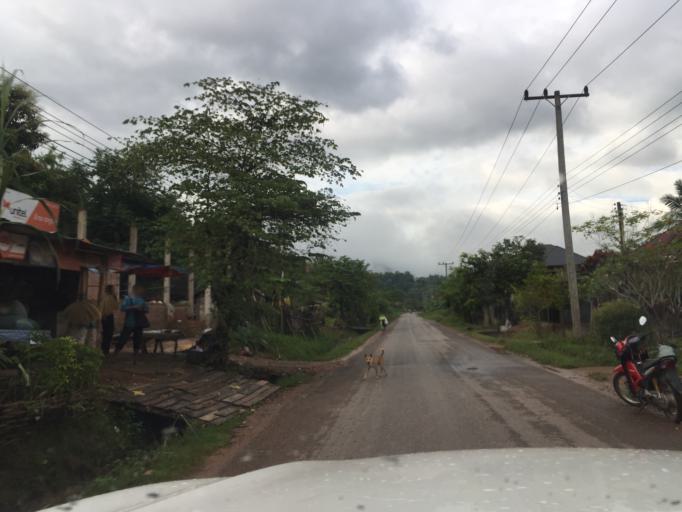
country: LA
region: Oudomxai
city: Muang La
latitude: 20.8567
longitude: 102.1105
